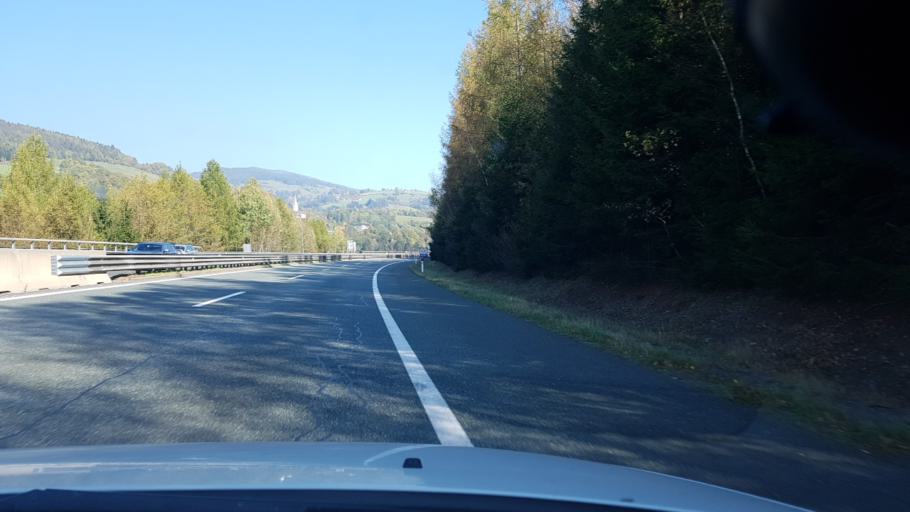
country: AT
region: Carinthia
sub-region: Politischer Bezirk Spittal an der Drau
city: Gmuend
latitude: 46.9060
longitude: 13.5442
